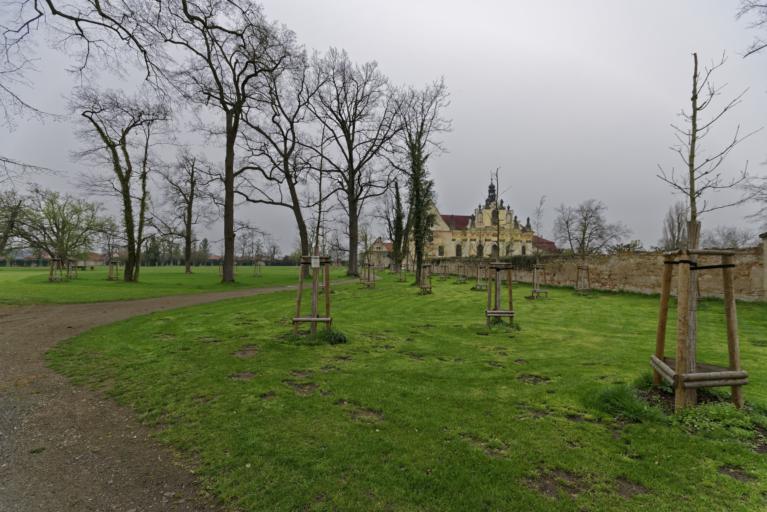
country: CZ
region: Central Bohemia
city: Mnichovo Hradiste
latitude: 50.5283
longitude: 14.9732
